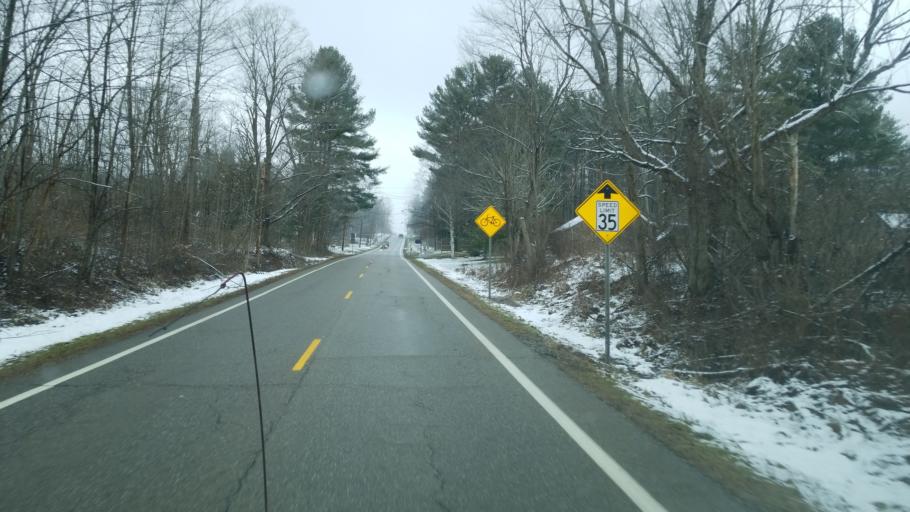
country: US
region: Ohio
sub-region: Portage County
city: Hiram
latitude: 41.3095
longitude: -81.1331
